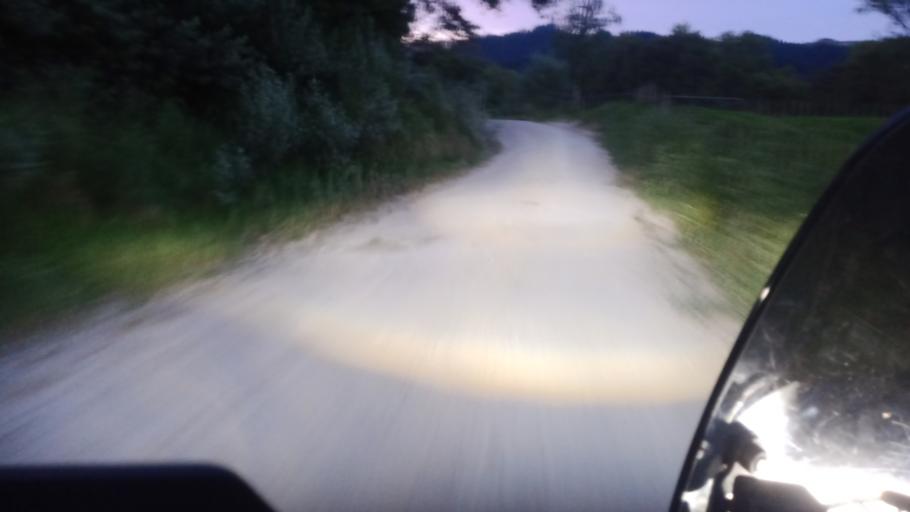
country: NZ
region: Gisborne
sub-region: Gisborne District
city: Gisborne
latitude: -38.4921
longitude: 177.9592
